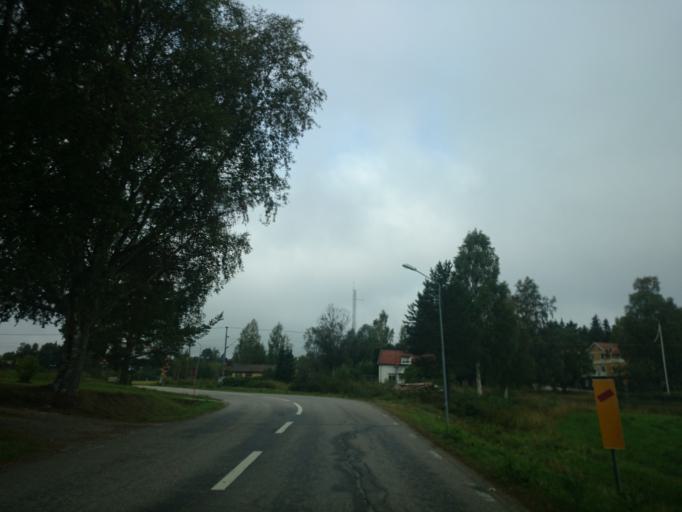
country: SE
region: Gaevleborg
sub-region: Nordanstigs Kommun
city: Bergsjoe
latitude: 61.9771
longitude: 17.2491
